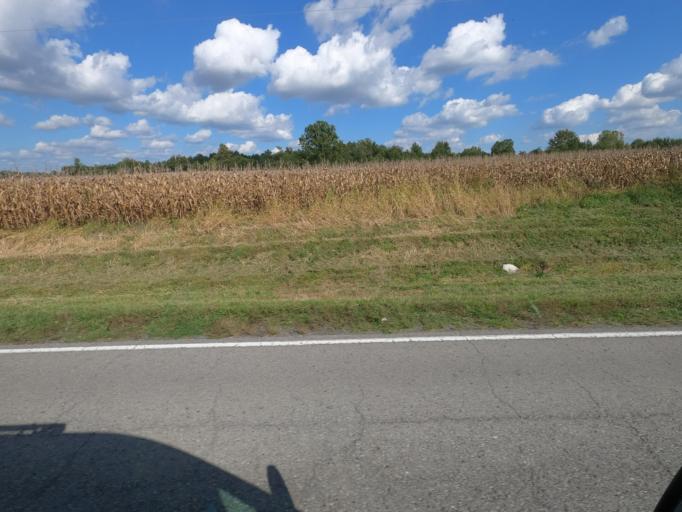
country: US
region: Illinois
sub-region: Massac County
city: Metropolis
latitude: 37.2788
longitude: -88.7560
